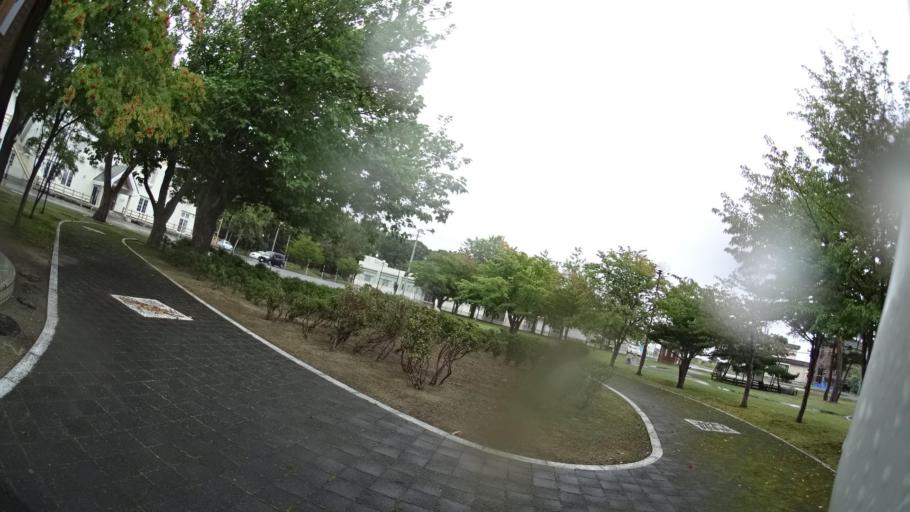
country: JP
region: Hokkaido
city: Kitami
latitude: 44.1887
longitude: 143.7365
